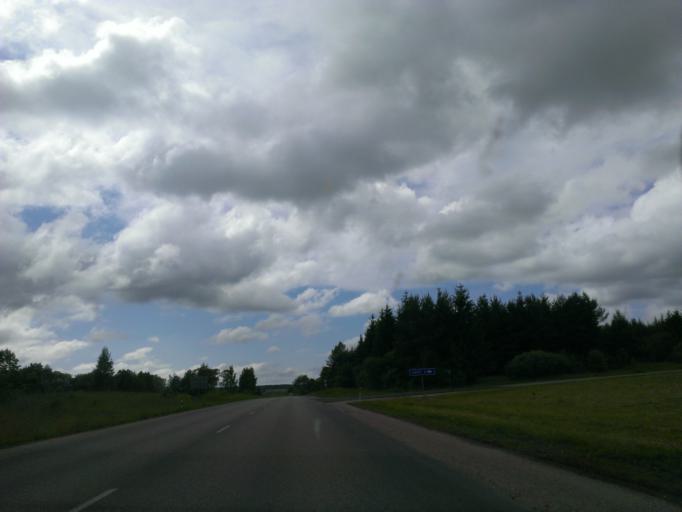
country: LV
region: Durbe
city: Liegi
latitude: 56.5917
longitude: 21.3725
